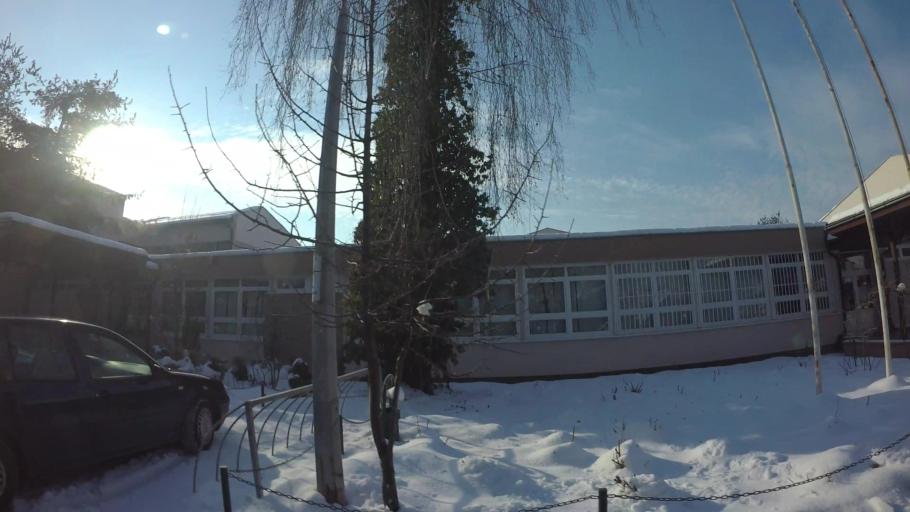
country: BA
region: Federation of Bosnia and Herzegovina
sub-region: Kanton Sarajevo
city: Sarajevo
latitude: 43.8361
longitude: 18.3379
